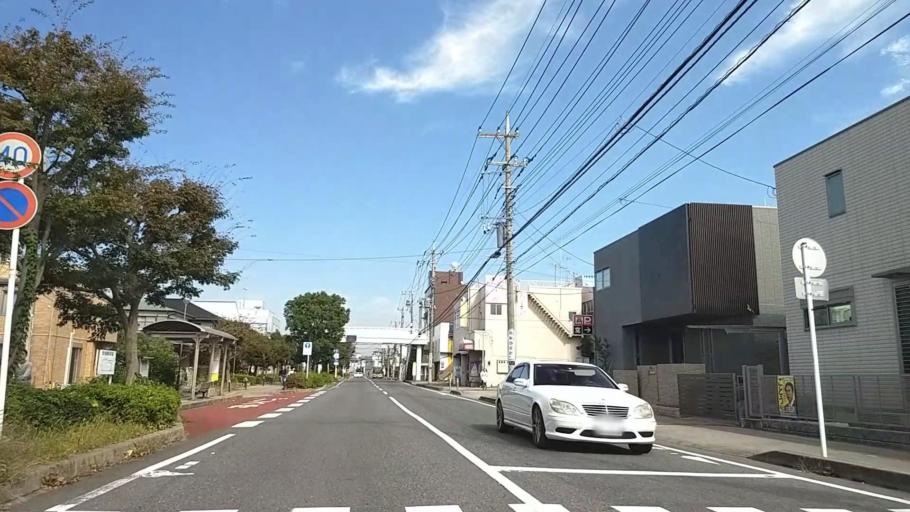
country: JP
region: Kanagawa
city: Atsugi
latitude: 35.4453
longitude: 139.3610
